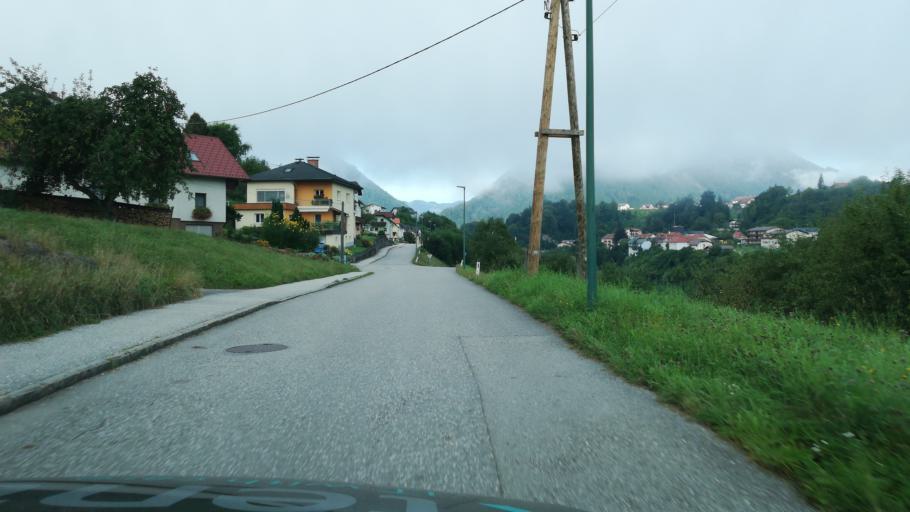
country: AT
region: Upper Austria
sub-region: Politischer Bezirk Steyr-Land
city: Maria Neustift
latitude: 47.8810
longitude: 14.5553
